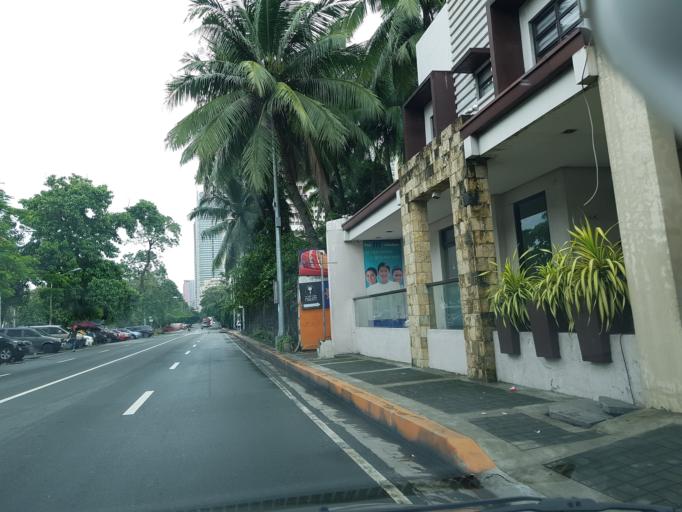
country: PH
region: Metro Manila
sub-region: City of Manila
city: Port Area
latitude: 14.5699
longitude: 120.9828
